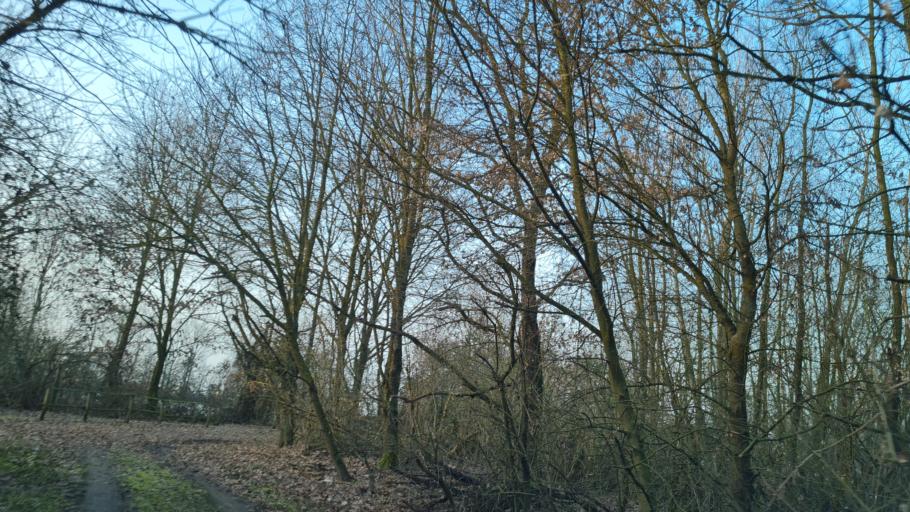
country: IT
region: Piedmont
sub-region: Provincia di Novara
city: Casalbeltrame
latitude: 45.4235
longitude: 8.5068
